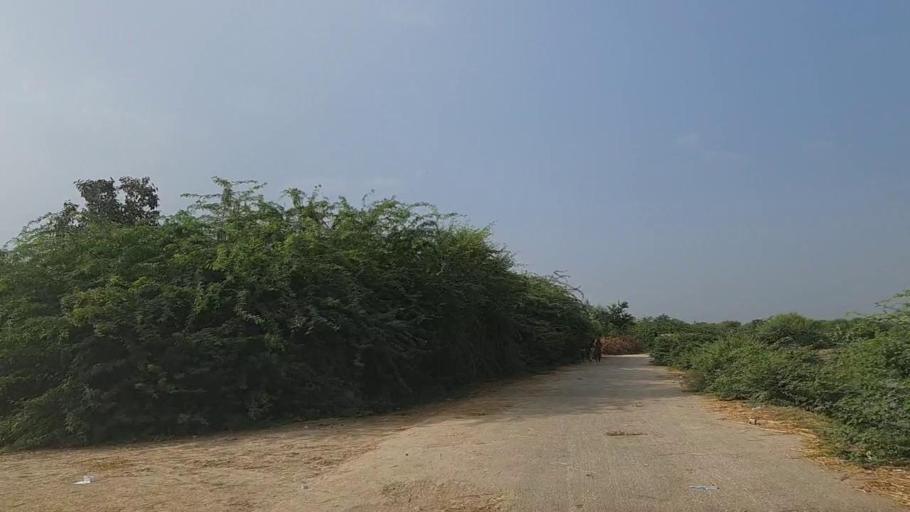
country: PK
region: Sindh
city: Daro Mehar
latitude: 24.7201
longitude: 68.1576
